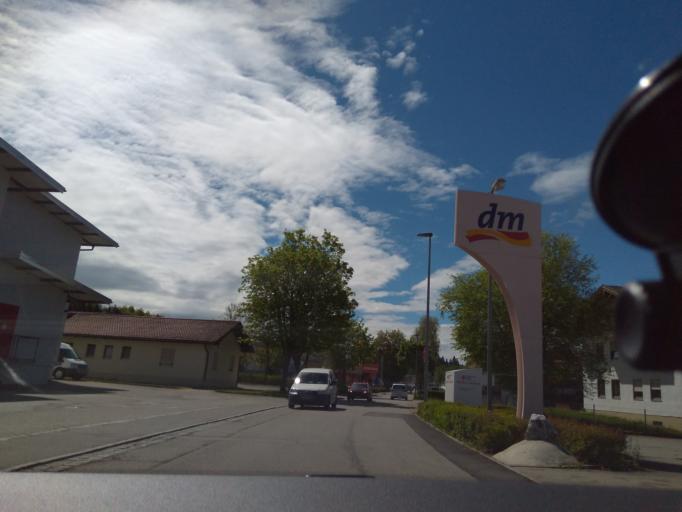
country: DE
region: Bavaria
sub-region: Upper Bavaria
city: Bad Endorf
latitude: 47.9189
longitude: 12.2945
